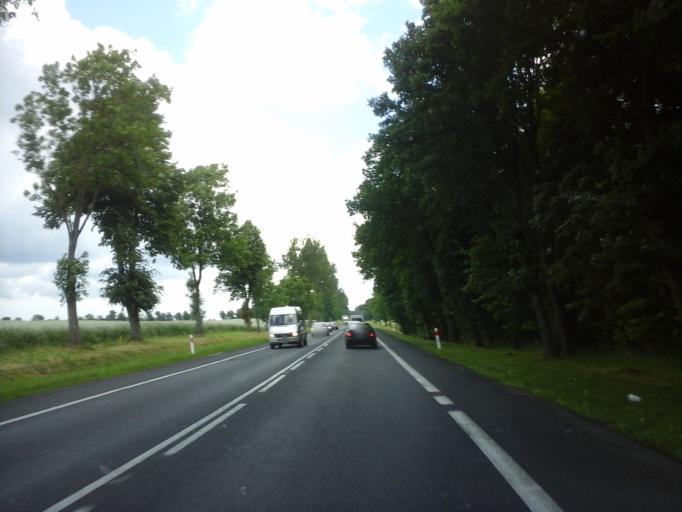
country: PL
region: West Pomeranian Voivodeship
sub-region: Powiat bialogardzki
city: Bialogard
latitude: 54.0924
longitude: 15.9913
